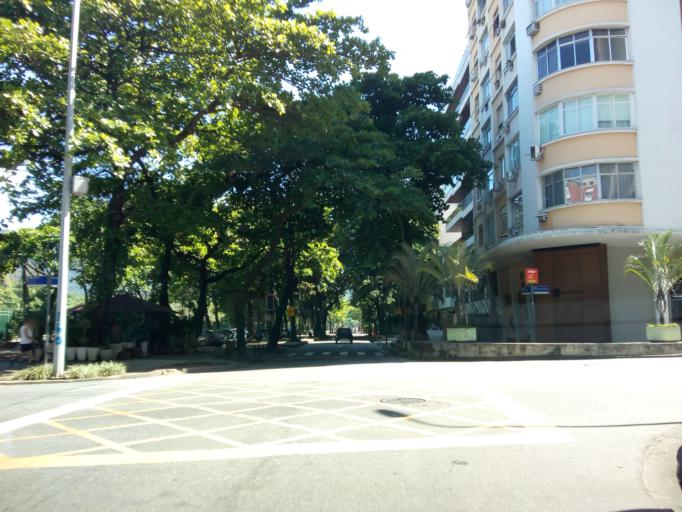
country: BR
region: Rio de Janeiro
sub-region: Rio De Janeiro
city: Rio de Janeiro
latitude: -22.9840
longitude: -43.2146
